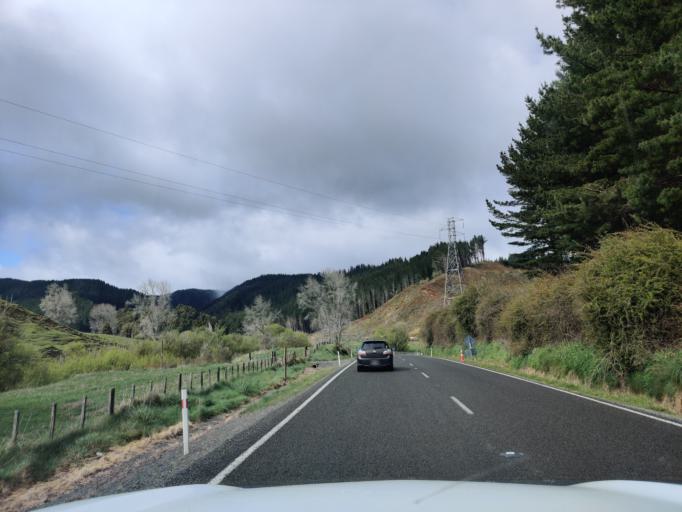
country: NZ
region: Waikato
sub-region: Otorohanga District
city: Otorohanga
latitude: -38.6134
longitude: 175.2191
